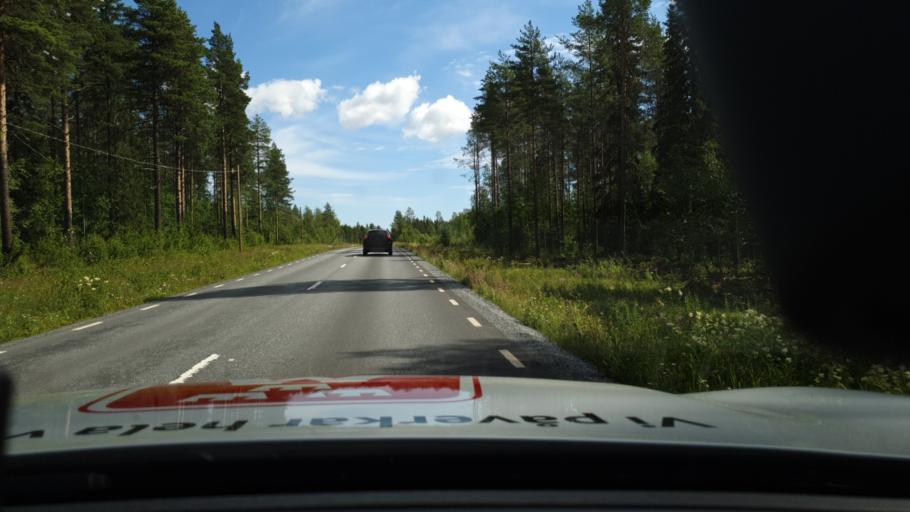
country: SE
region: Norrbotten
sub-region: Lulea Kommun
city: Ranea
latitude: 65.7904
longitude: 22.1346
